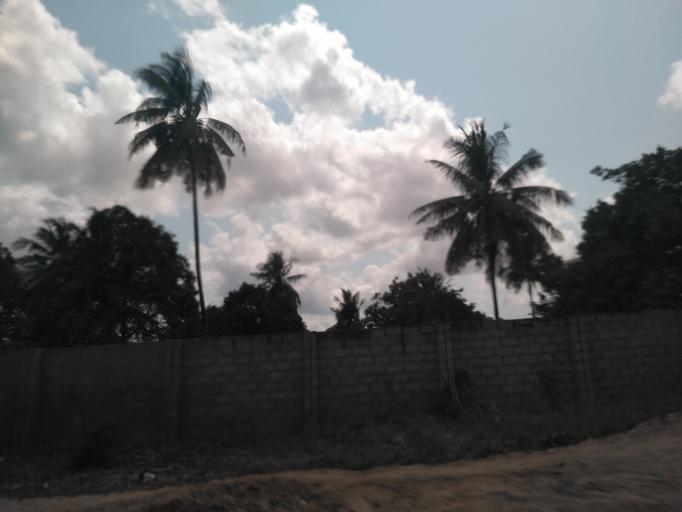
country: TZ
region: Dar es Salaam
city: Dar es Salaam
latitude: -6.8787
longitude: 39.3366
